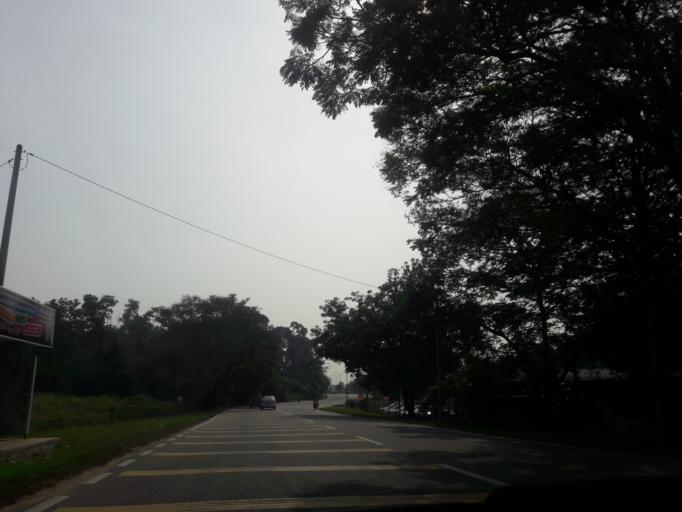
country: MY
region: Kedah
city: Kulim
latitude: 5.3493
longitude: 100.5249
